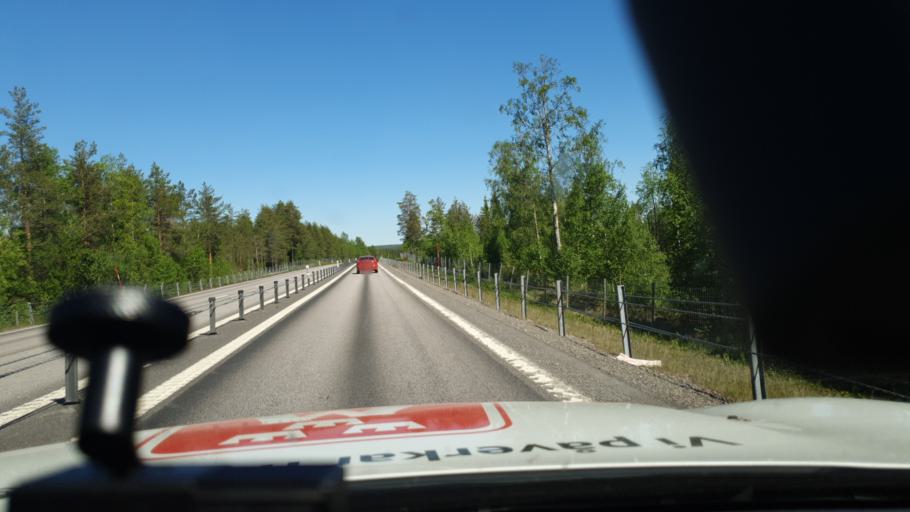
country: SE
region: Norrbotten
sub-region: Kalix Kommun
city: Toere
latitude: 65.8944
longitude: 22.5925
